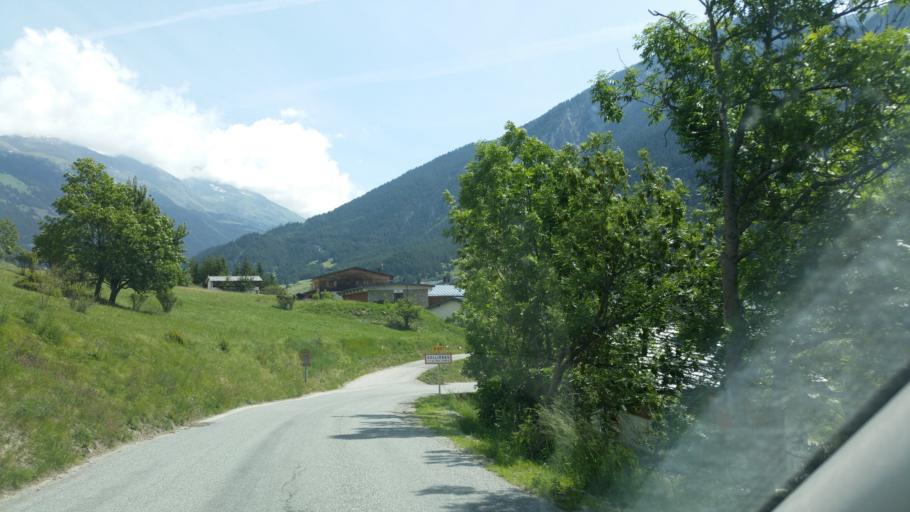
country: FR
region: Rhone-Alpes
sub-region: Departement de la Savoie
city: Modane
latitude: 45.2644
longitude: 6.8062
